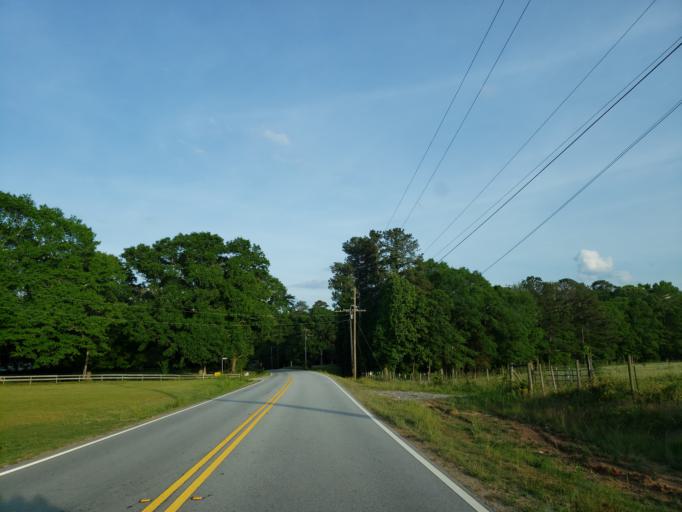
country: US
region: Georgia
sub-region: Carroll County
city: Mount Zion
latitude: 33.6069
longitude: -85.1465
